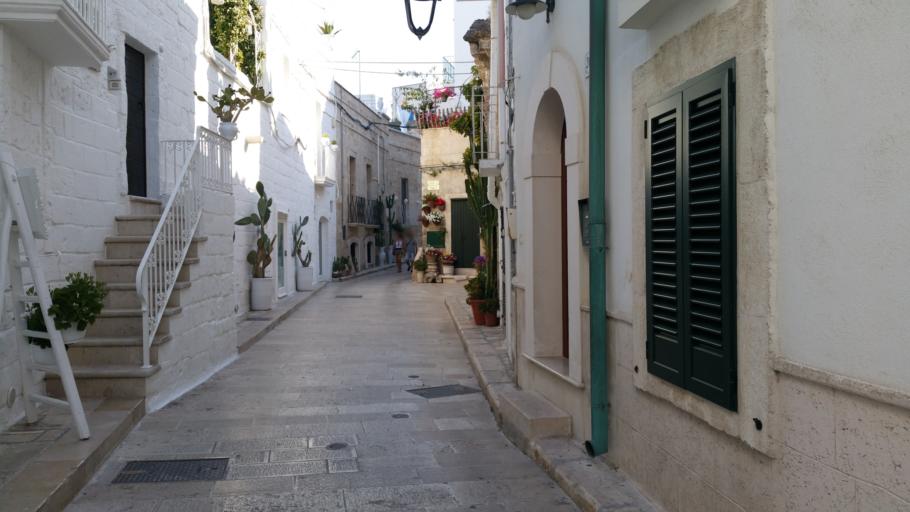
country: IT
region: Apulia
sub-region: Provincia di Bari
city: Monopoli
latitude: 40.9522
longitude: 17.3064
